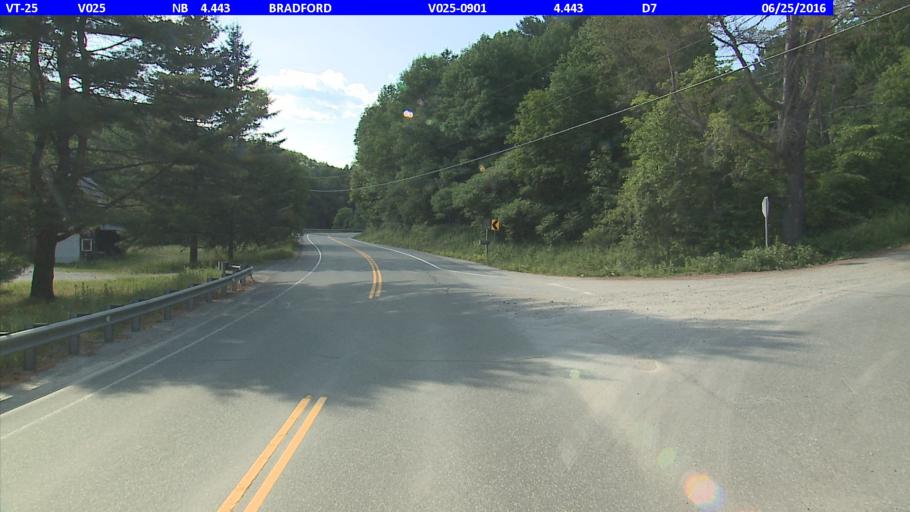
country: US
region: New Hampshire
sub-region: Grafton County
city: Haverhill
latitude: 44.0170
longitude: -72.1715
